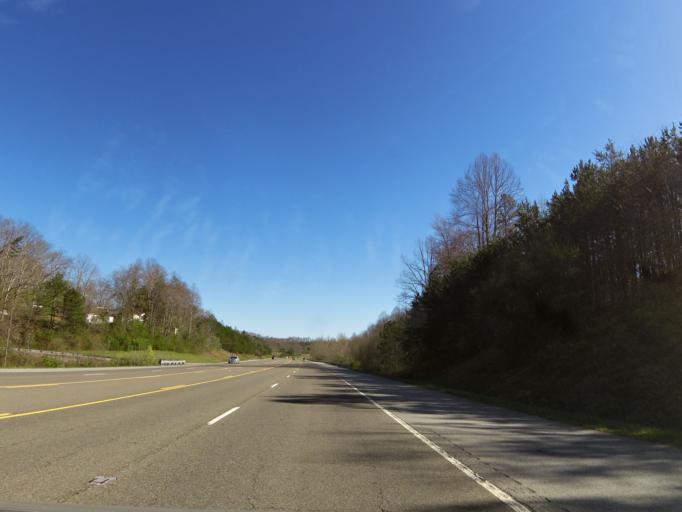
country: US
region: Tennessee
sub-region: Scott County
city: Oneida
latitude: 36.4526
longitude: -84.5447
